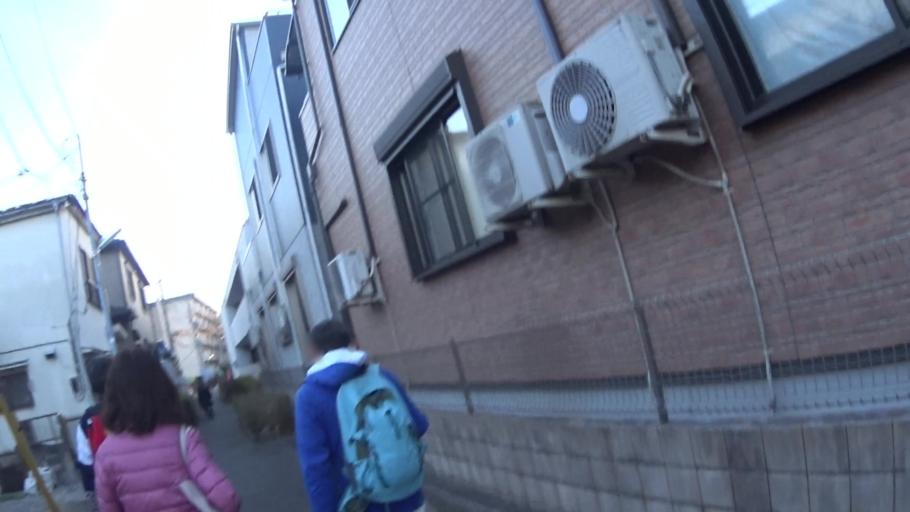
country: JP
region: Saitama
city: Saitama
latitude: 35.9238
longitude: 139.6268
